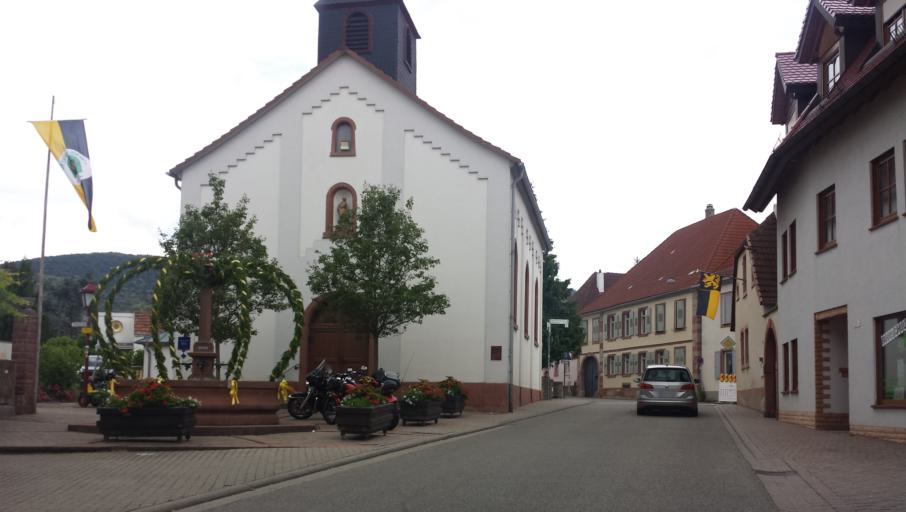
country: DE
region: Rheinland-Pfalz
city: Maikammer
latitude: 49.3084
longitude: 8.1230
